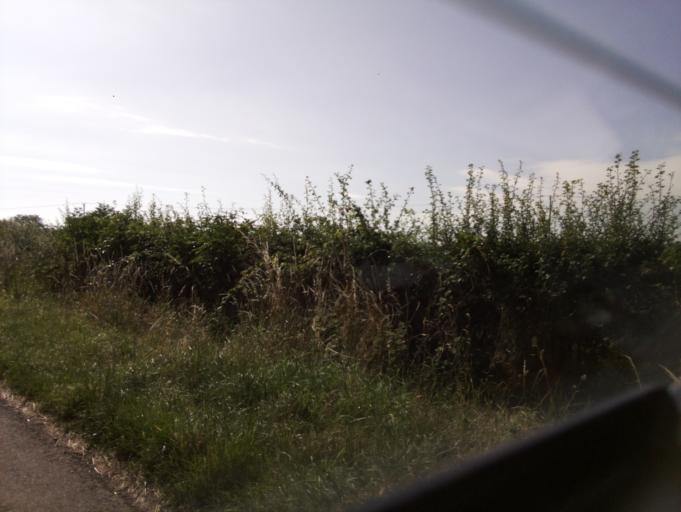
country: GB
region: England
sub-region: Oxfordshire
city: Ducklington
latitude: 51.7232
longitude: -1.4984
